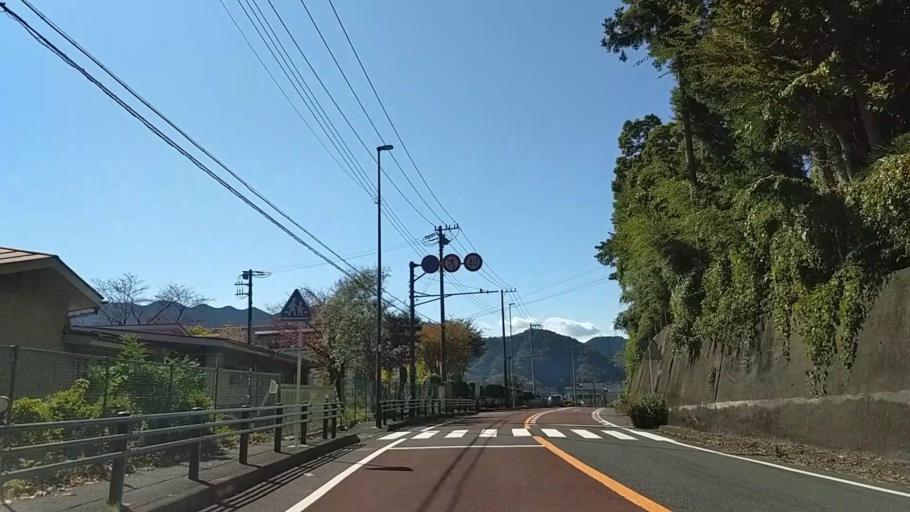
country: JP
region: Yamanashi
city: Uenohara
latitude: 35.6170
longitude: 139.1942
